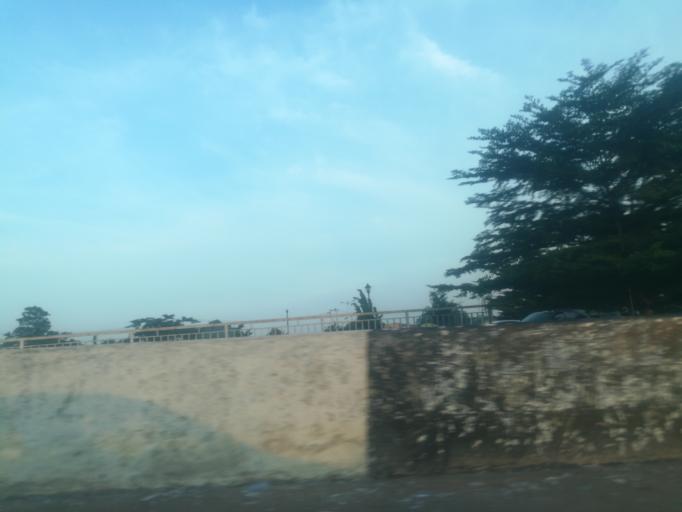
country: NG
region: Ogun
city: Abeokuta
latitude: 7.1478
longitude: 3.3287
